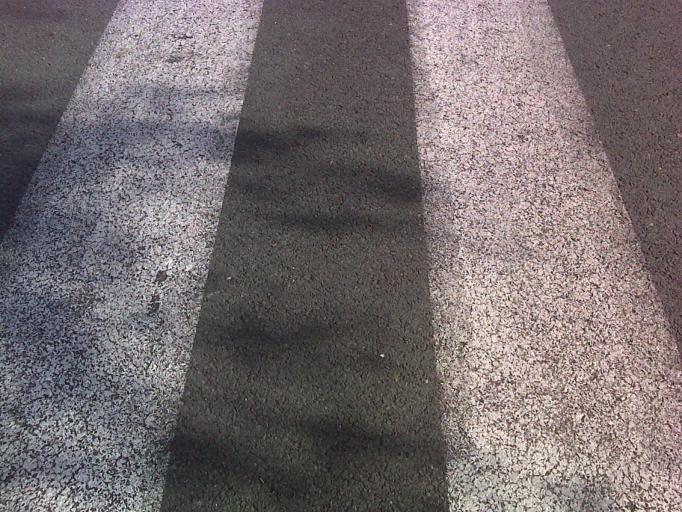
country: FR
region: Poitou-Charentes
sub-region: Departement de la Charente-Maritime
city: Marennes
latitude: 45.8128
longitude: -1.1128
